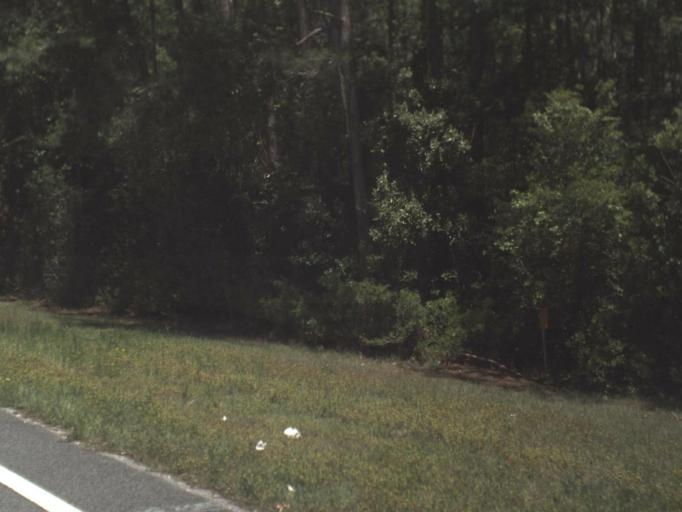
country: US
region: Florida
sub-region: Escambia County
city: Warrington
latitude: 30.3438
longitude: -87.3496
